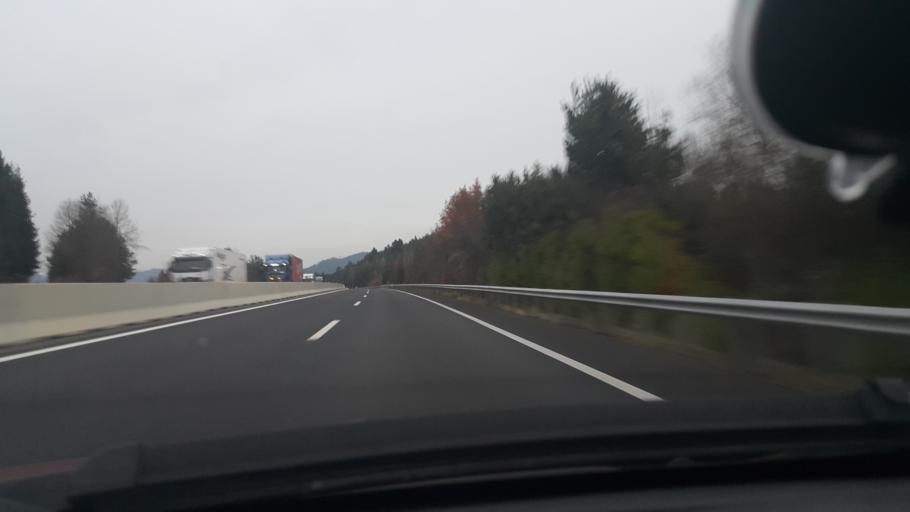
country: AT
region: Carinthia
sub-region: Politischer Bezirk Volkermarkt
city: Voelkermarkt
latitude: 46.6829
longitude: 14.6780
